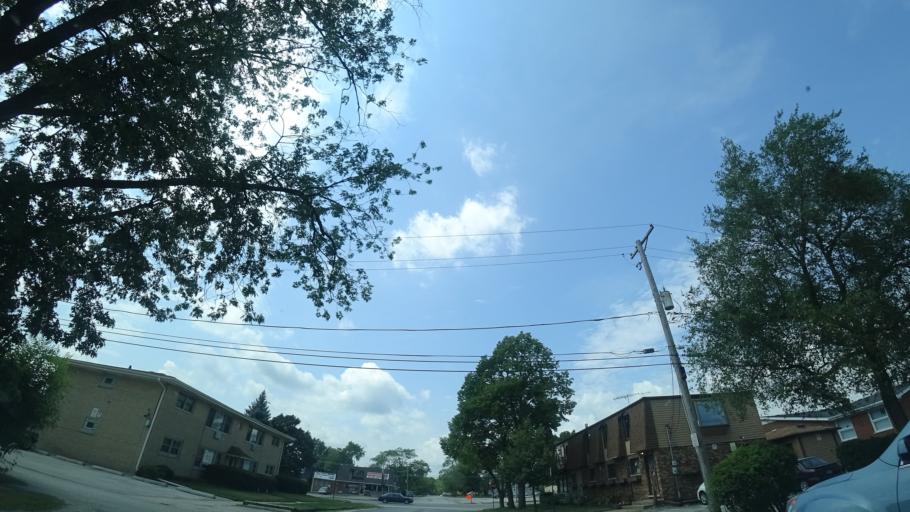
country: US
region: Illinois
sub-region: Cook County
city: Worth
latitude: 41.6852
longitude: -87.7965
